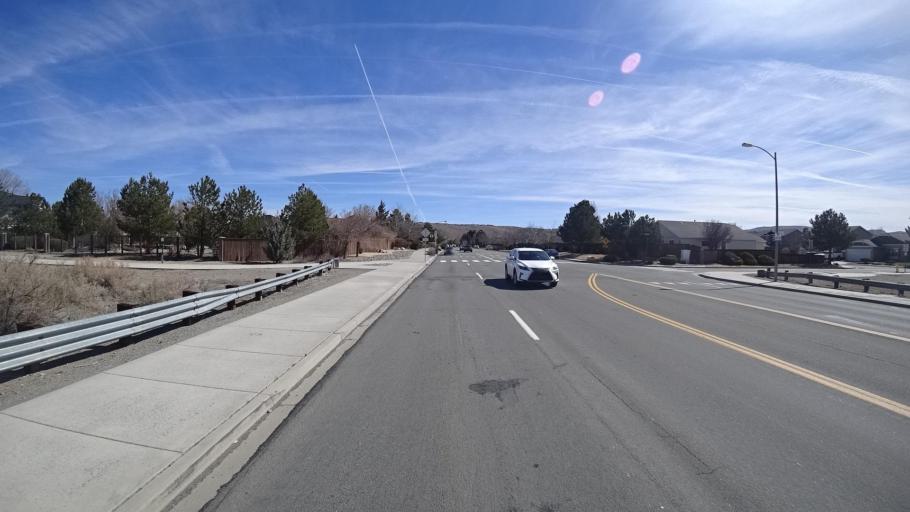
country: US
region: Nevada
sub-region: Washoe County
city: Sun Valley
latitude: 39.5856
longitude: -119.7297
